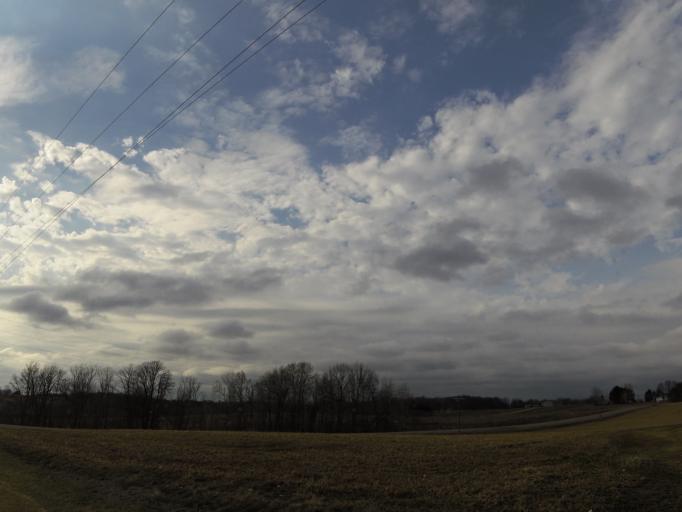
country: US
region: Wisconsin
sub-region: Pierce County
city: Ellsworth
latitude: 44.7468
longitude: -92.4659
